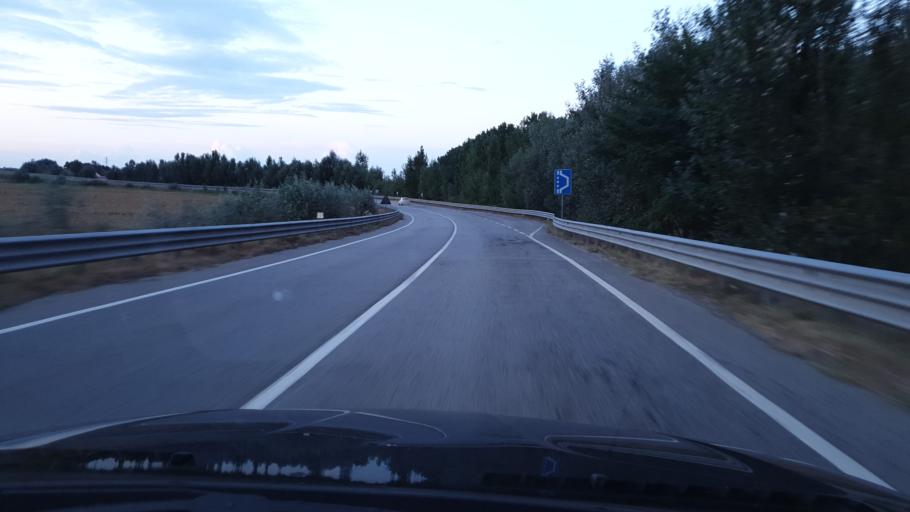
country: IT
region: Emilia-Romagna
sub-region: Provincia di Ravenna
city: Alfonsine
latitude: 44.5005
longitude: 12.0608
